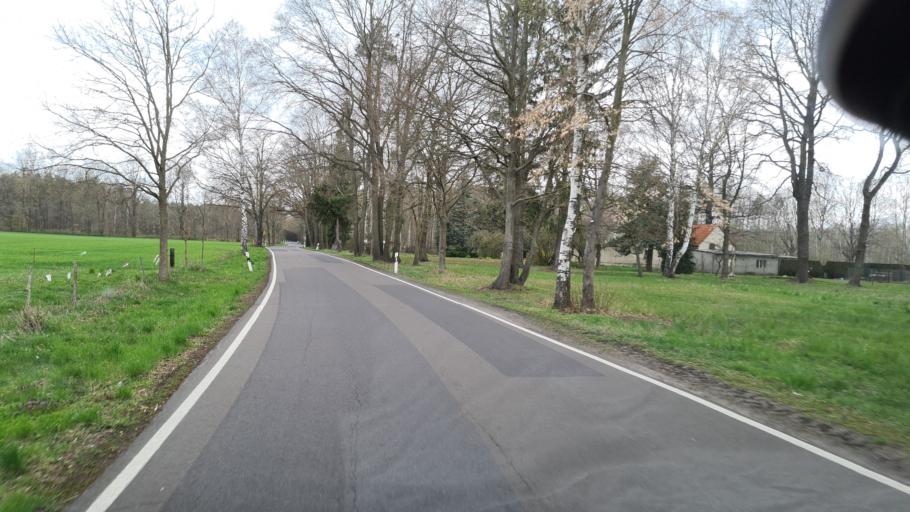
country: DE
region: Brandenburg
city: Schwarzbach
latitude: 51.4549
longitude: 13.9290
